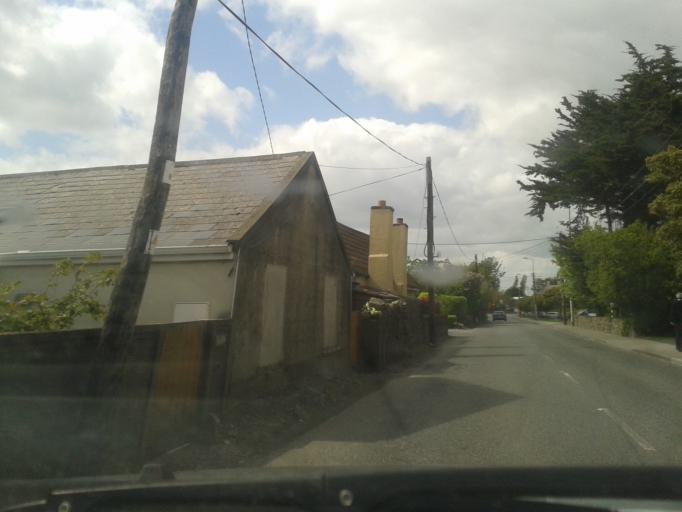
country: IE
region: Leinster
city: Cabinteely
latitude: 53.2783
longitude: -6.1553
